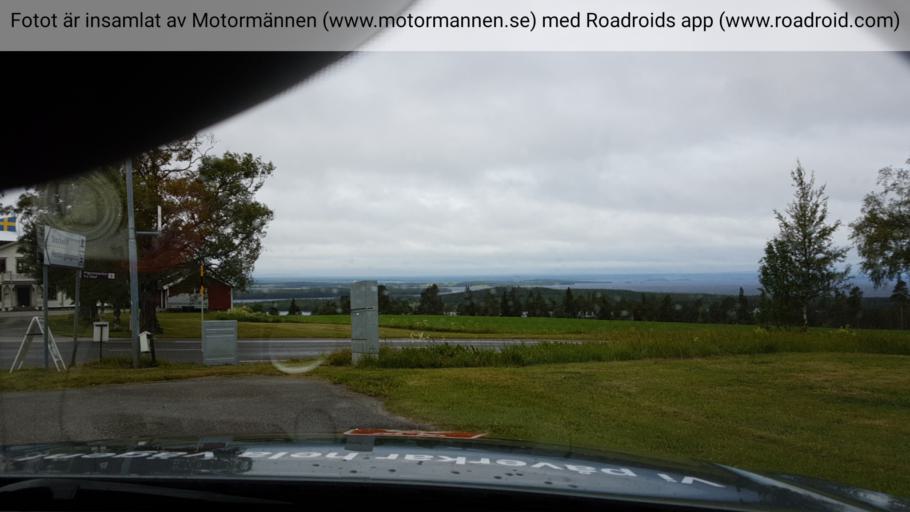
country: SE
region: Jaemtland
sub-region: OEstersunds Kommun
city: Ostersund
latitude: 63.1856
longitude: 14.5067
